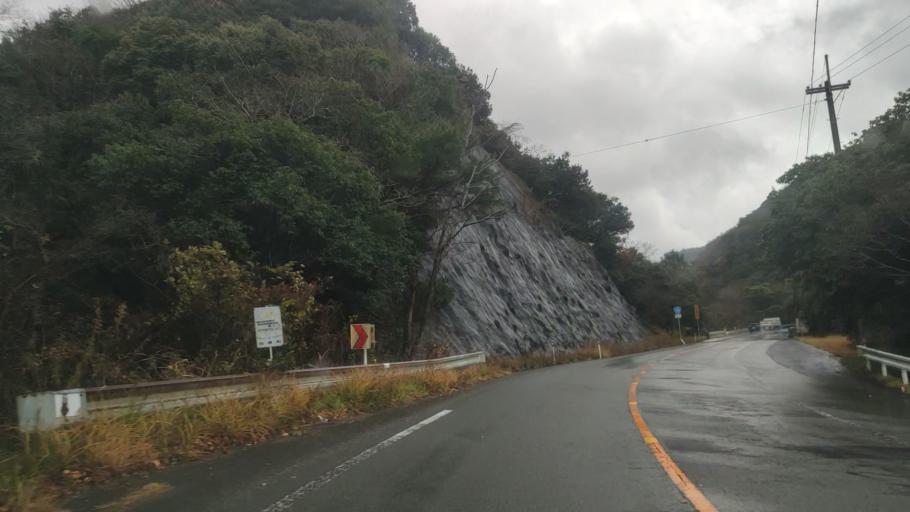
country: JP
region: Tokushima
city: Kamojimacho-jogejima
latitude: 34.1884
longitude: 134.3366
